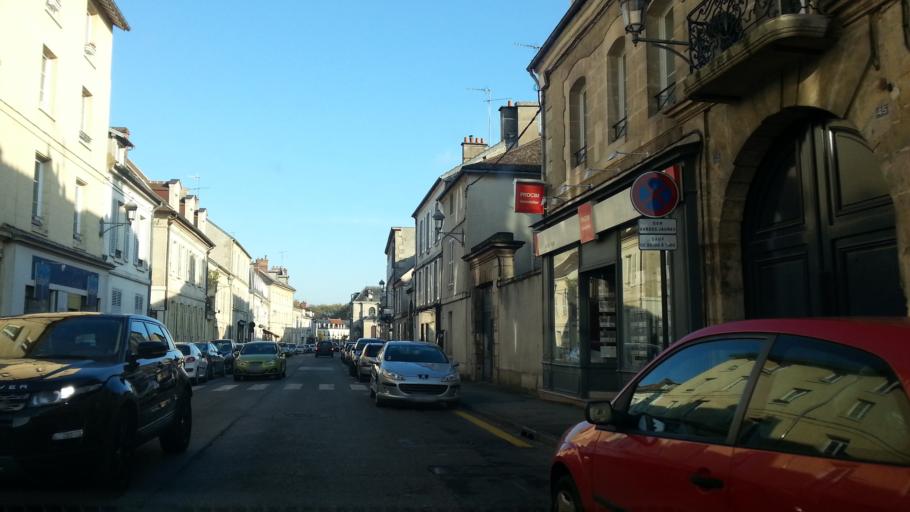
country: FR
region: Picardie
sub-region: Departement de l'Oise
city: Chantilly
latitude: 49.1944
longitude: 2.4745
